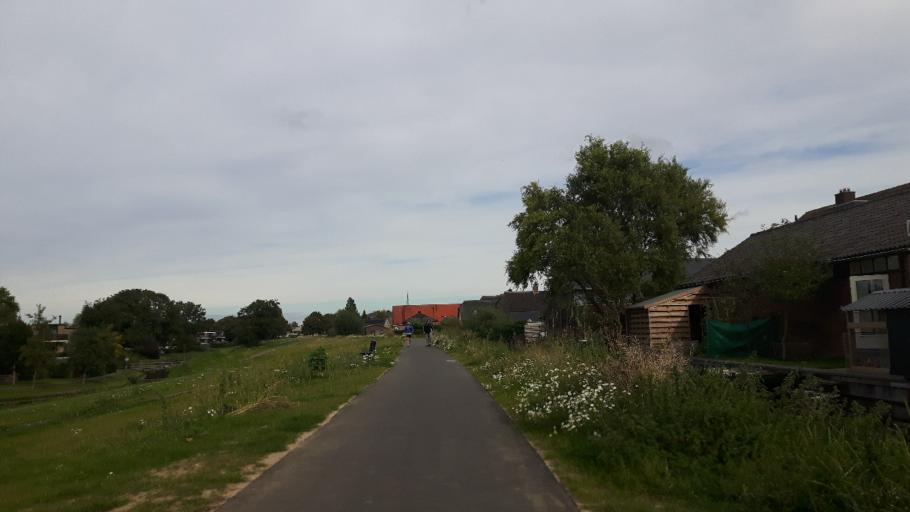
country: NL
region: South Holland
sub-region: Gemeente Nieuwkoop
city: Nieuwkoop
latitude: 52.1435
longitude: 4.7714
